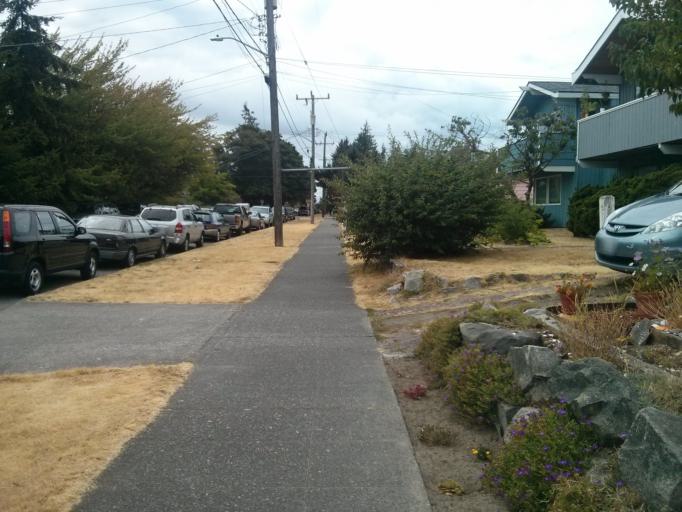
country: US
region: Washington
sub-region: King County
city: White Center
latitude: 47.5769
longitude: -122.4122
